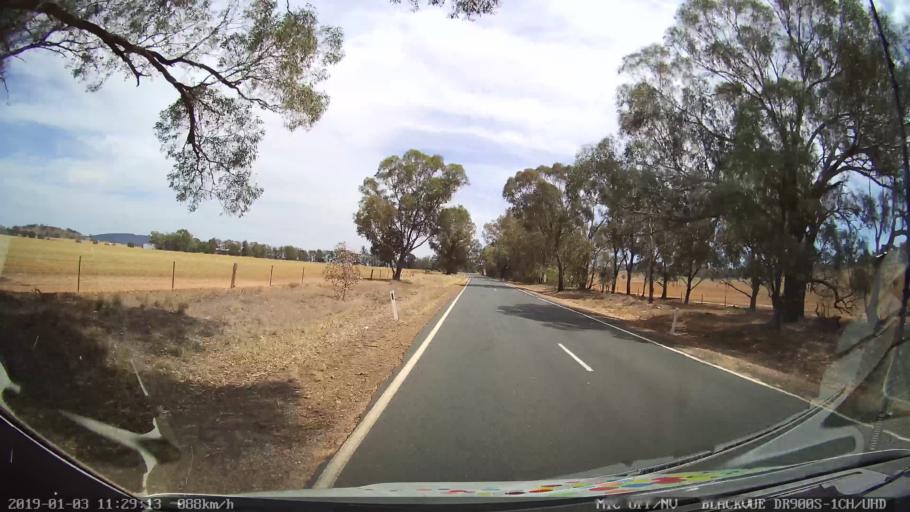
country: AU
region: New South Wales
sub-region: Weddin
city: Grenfell
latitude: -33.9945
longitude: 148.2008
